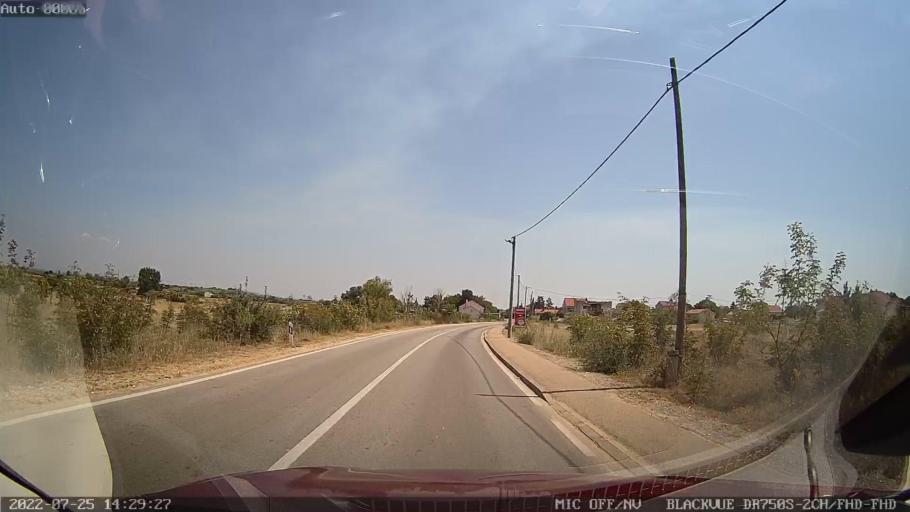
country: HR
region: Zadarska
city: Policnik
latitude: 44.1201
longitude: 15.3564
